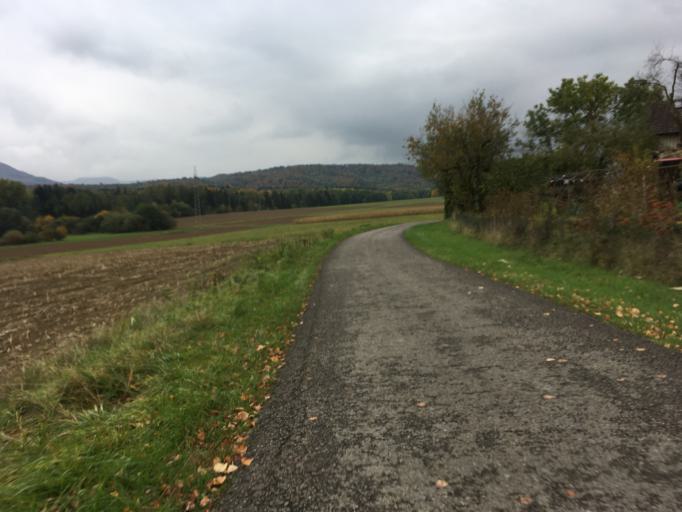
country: DE
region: Baden-Wuerttemberg
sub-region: Tuebingen Region
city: Gomaringen
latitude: 48.4422
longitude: 9.0849
